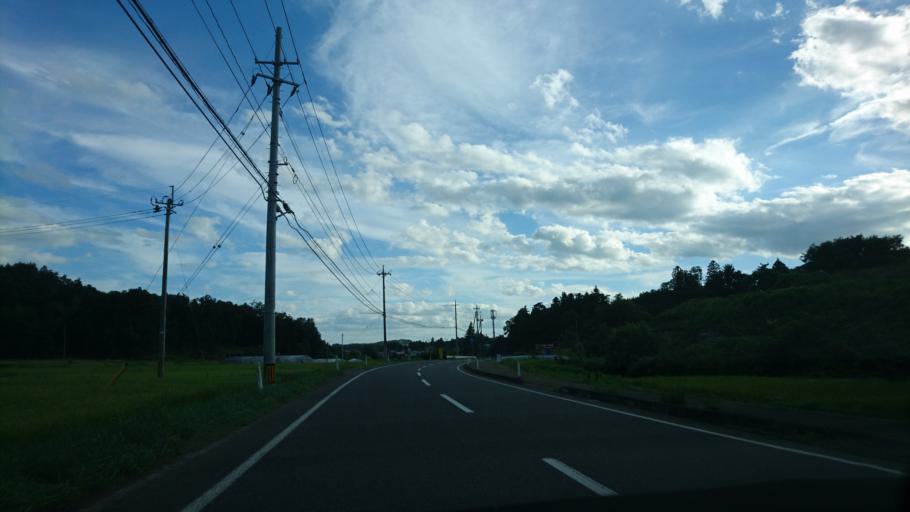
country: JP
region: Iwate
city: Ichinoseki
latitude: 38.8540
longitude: 141.1824
